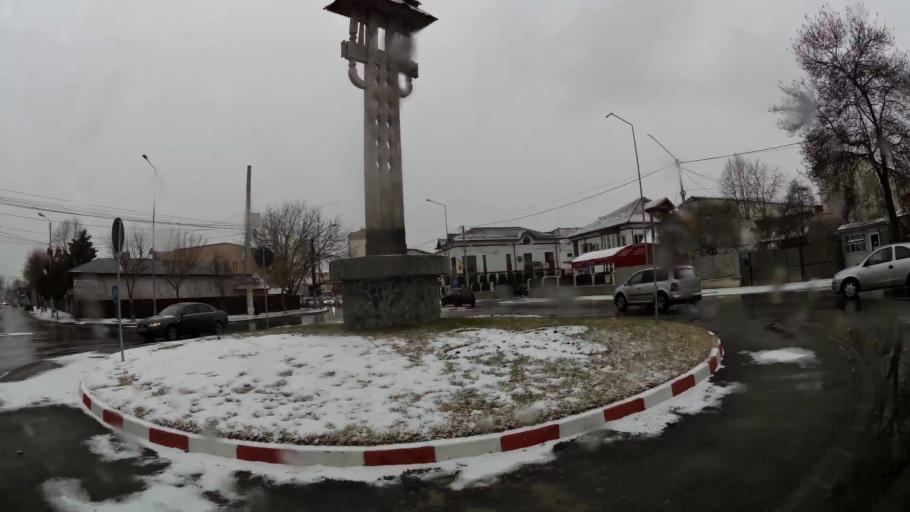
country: RO
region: Dambovita
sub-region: Municipiul Targoviste
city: Targoviste
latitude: 44.9274
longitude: 25.4452
